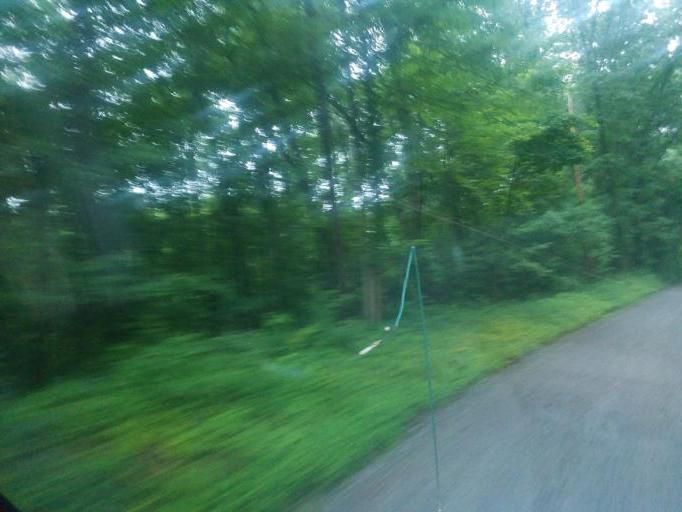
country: US
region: Ohio
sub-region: Columbiana County
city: Salineville
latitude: 40.6213
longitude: -80.8957
